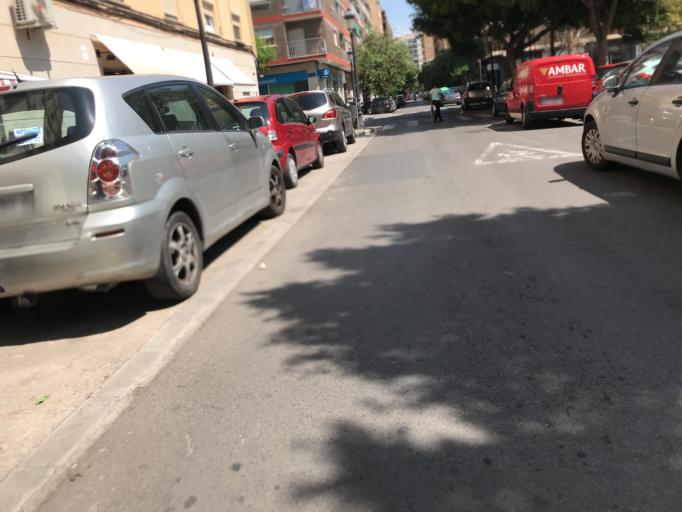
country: ES
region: Valencia
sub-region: Provincia de Valencia
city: Valencia
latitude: 39.4678
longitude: -0.3476
